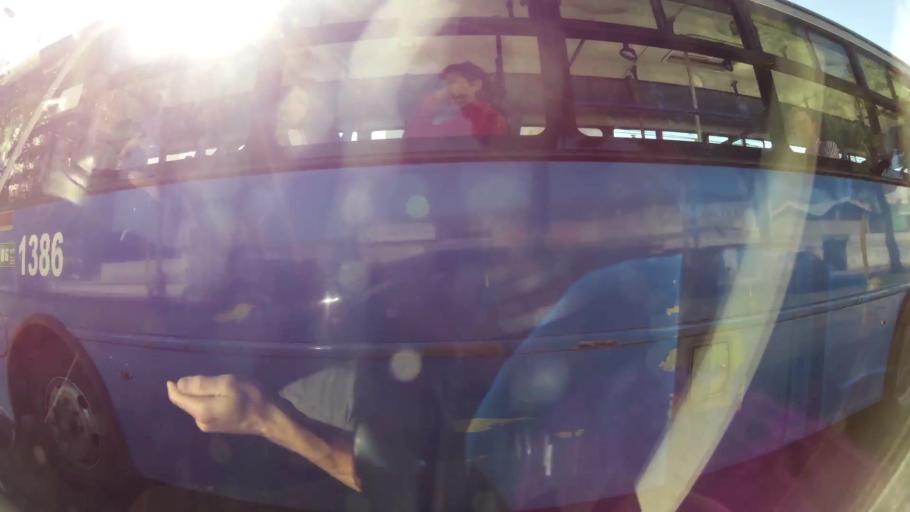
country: EC
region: Pichincha
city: Quito
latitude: -0.1441
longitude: -78.4745
